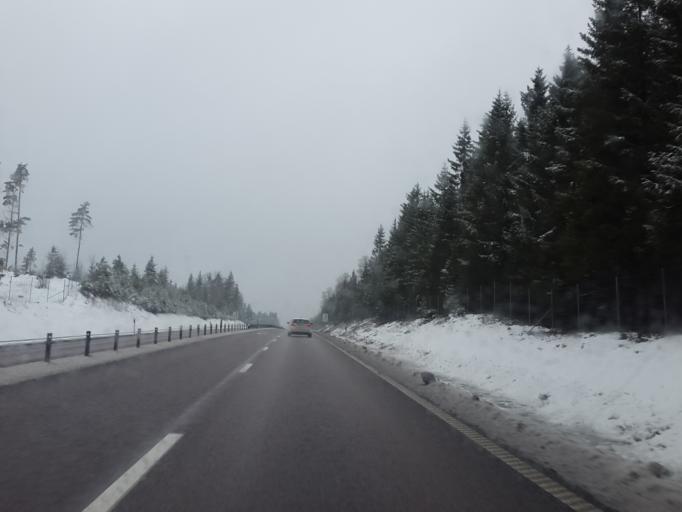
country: SE
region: Vaestra Goetaland
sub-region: Ulricehamns Kommun
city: Ulricehamn
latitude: 57.7851
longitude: 13.6448
